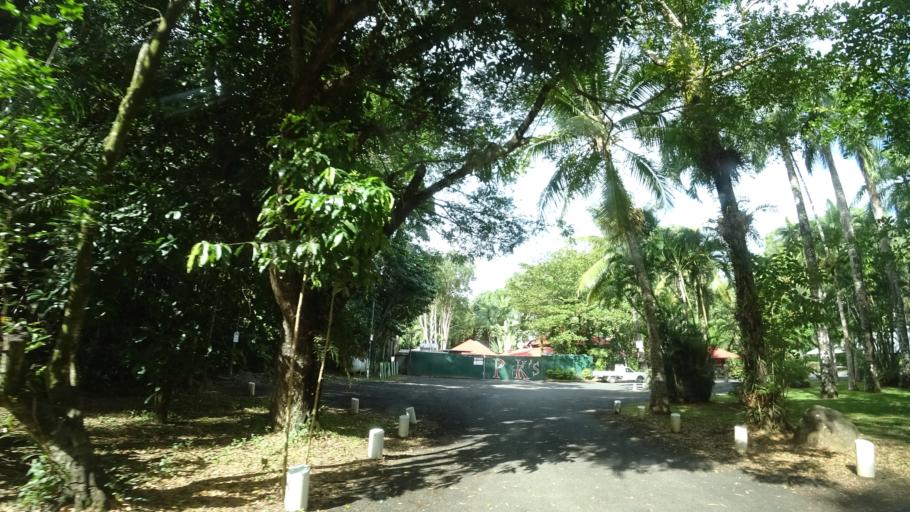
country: AU
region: Queensland
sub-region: Cairns
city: Port Douglas
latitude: -16.0866
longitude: 145.4630
